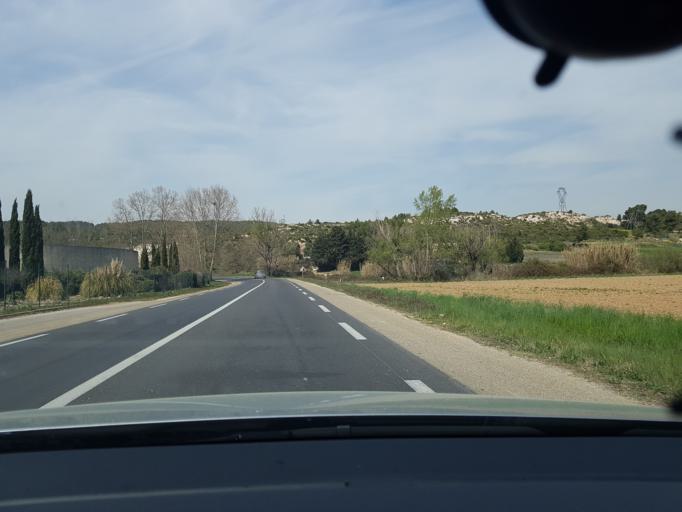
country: FR
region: Provence-Alpes-Cote d'Azur
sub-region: Departement des Bouches-du-Rhone
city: Gardanne
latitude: 43.4693
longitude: 5.4611
